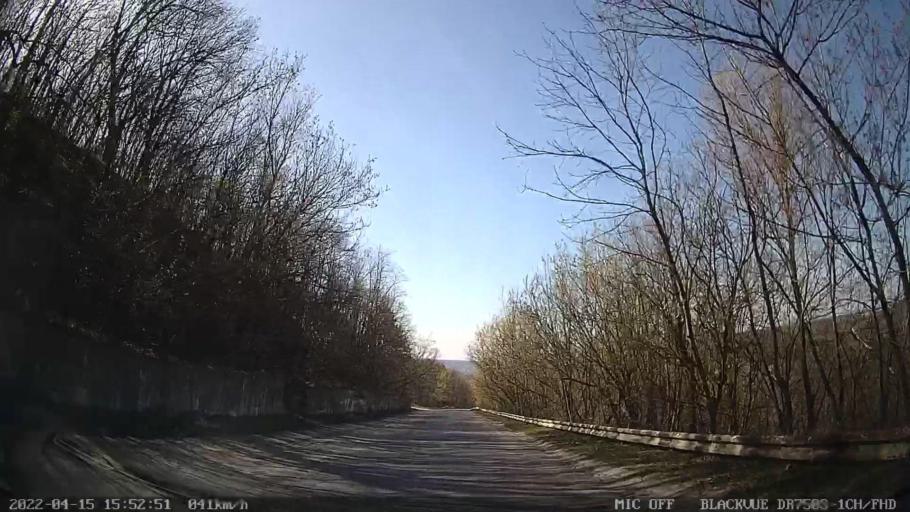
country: MD
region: Raionul Ocnita
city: Otaci
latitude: 48.3964
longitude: 27.8899
